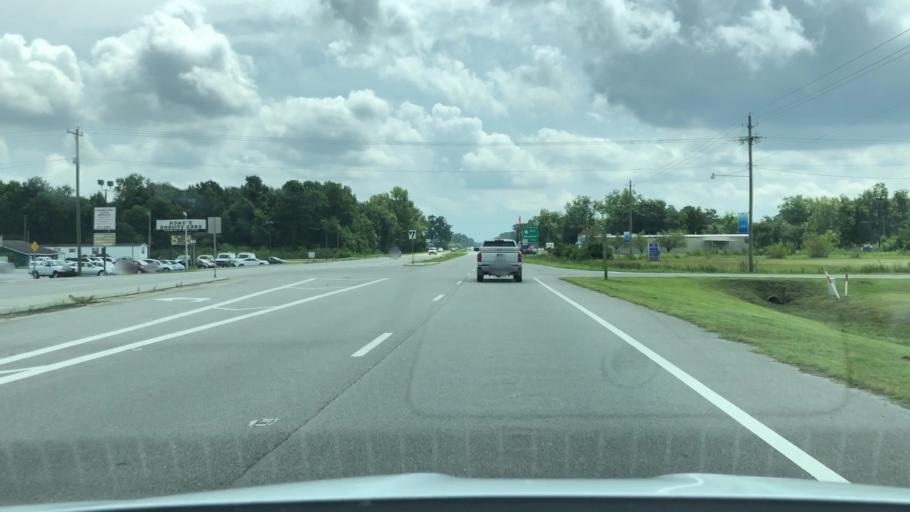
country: US
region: North Carolina
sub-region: Craven County
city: New Bern
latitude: 35.1279
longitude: -77.0250
